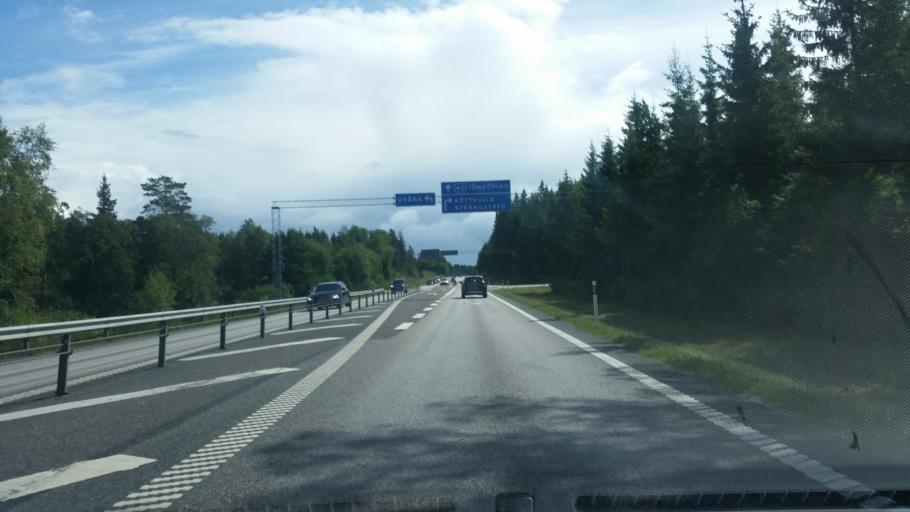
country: SE
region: Joenkoeping
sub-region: Mullsjo Kommun
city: Mullsjoe
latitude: 57.7754
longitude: 13.6828
